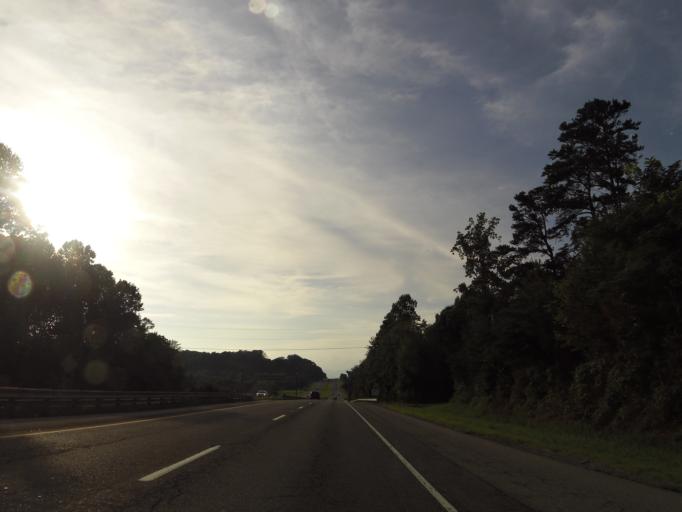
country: US
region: Tennessee
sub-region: Knox County
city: Farragut
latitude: 35.9325
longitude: -84.1419
